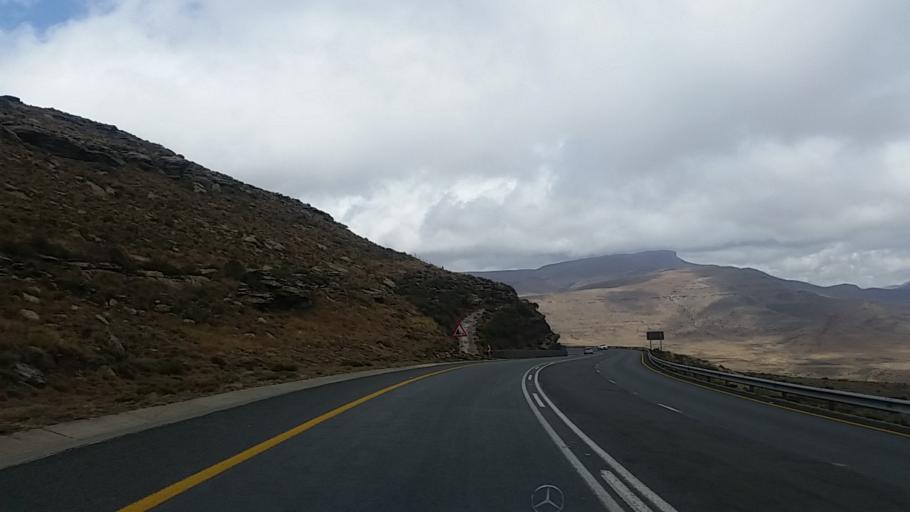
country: ZA
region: Eastern Cape
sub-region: Chris Hani District Municipality
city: Middelburg
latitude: -31.8373
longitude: 24.8614
